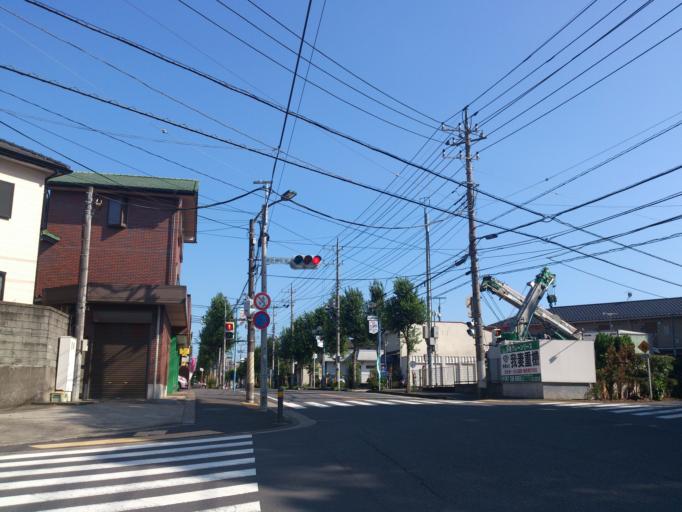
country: JP
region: Chiba
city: Matsudo
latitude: 35.7977
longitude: 139.9157
